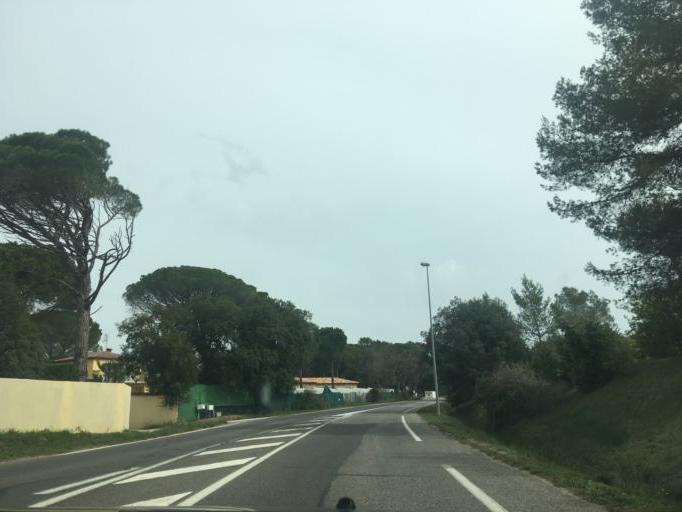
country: FR
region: Provence-Alpes-Cote d'Azur
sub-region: Departement du Var
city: Le Muy
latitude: 43.4986
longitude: 6.5789
